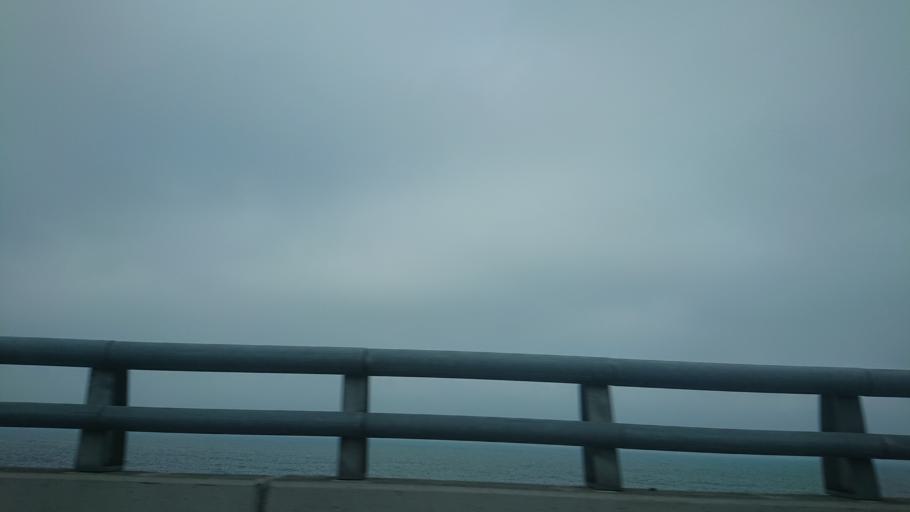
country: TW
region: Taiwan
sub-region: Miaoli
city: Miaoli
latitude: 24.5269
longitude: 120.6896
